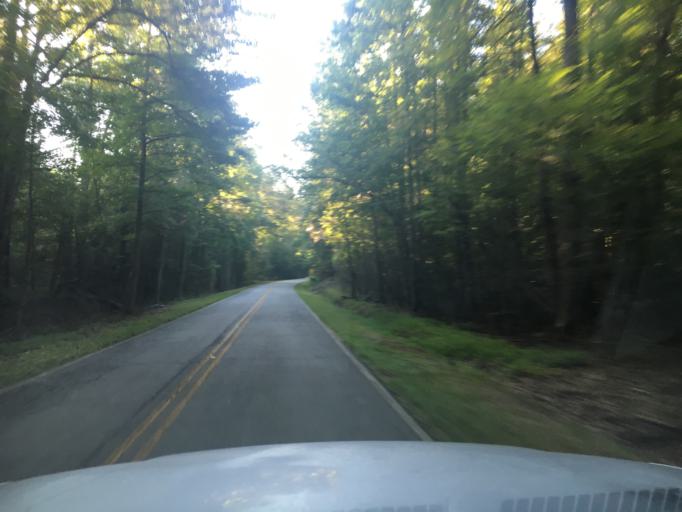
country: US
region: South Carolina
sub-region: Spartanburg County
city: Woodruff
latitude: 34.7707
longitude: -81.9667
